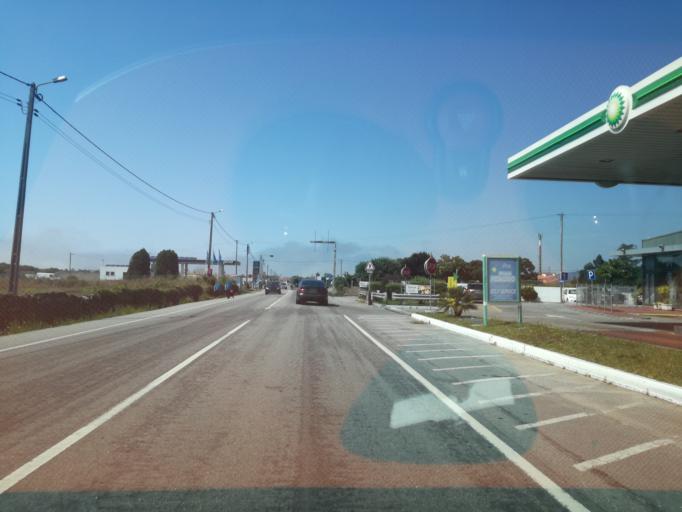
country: PT
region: Braga
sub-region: Esposende
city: Apulia
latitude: 41.5040
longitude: -8.7622
